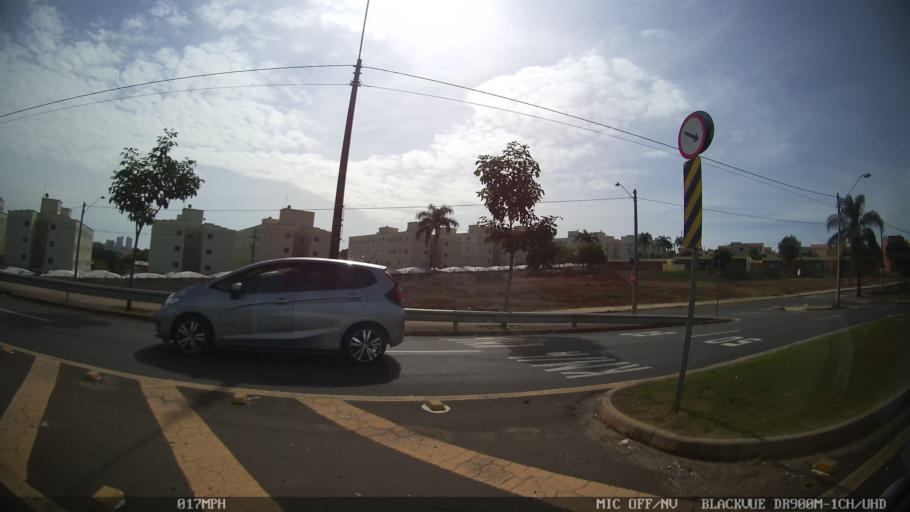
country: BR
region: Sao Paulo
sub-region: Piracicaba
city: Piracicaba
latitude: -22.7467
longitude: -47.6258
